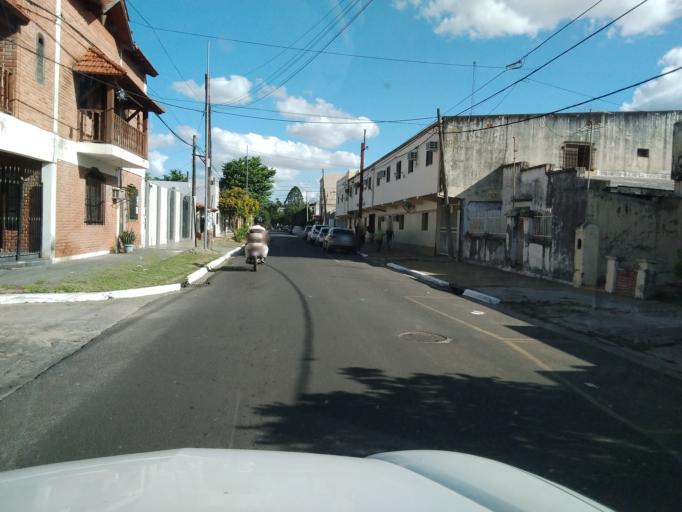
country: AR
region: Corrientes
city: Corrientes
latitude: -27.4828
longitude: -58.8322
